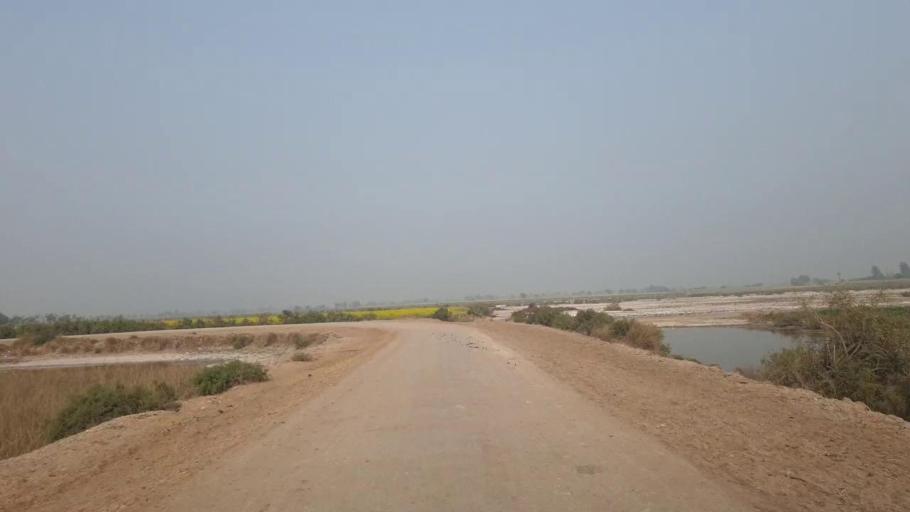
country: PK
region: Sindh
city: Shahdadpur
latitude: 25.8442
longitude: 68.5796
